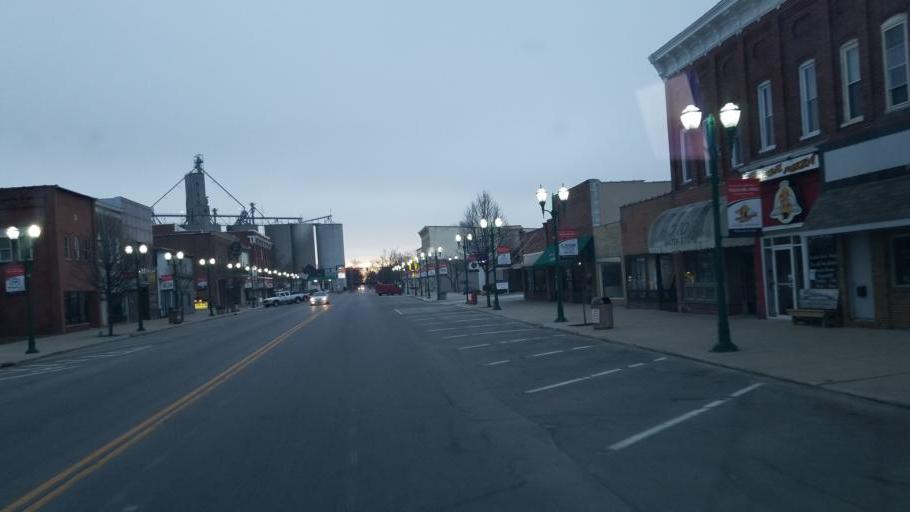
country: US
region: Ohio
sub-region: Defiance County
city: Hicksville
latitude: 41.2936
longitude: -84.7618
